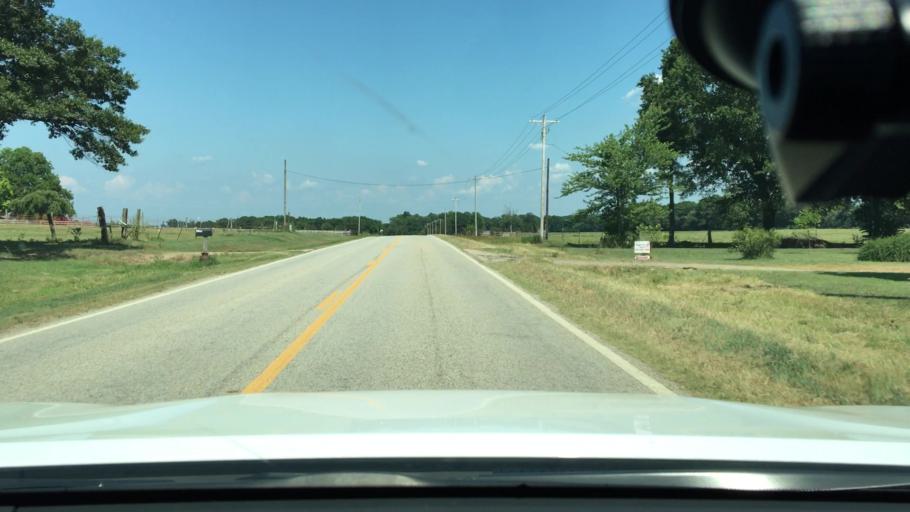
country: US
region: Arkansas
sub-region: Johnson County
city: Coal Hill
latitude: 35.3509
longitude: -93.5755
